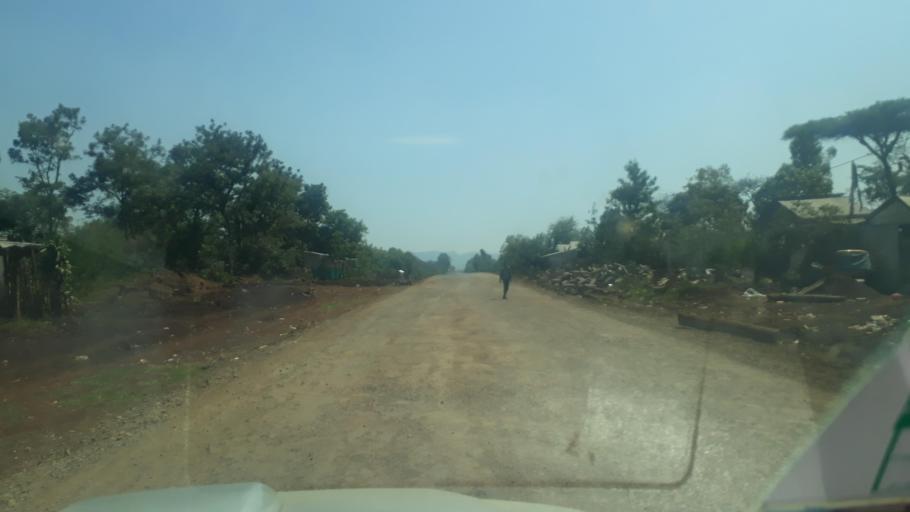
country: ET
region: Oromiya
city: Jima
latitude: 7.7275
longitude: 36.7934
